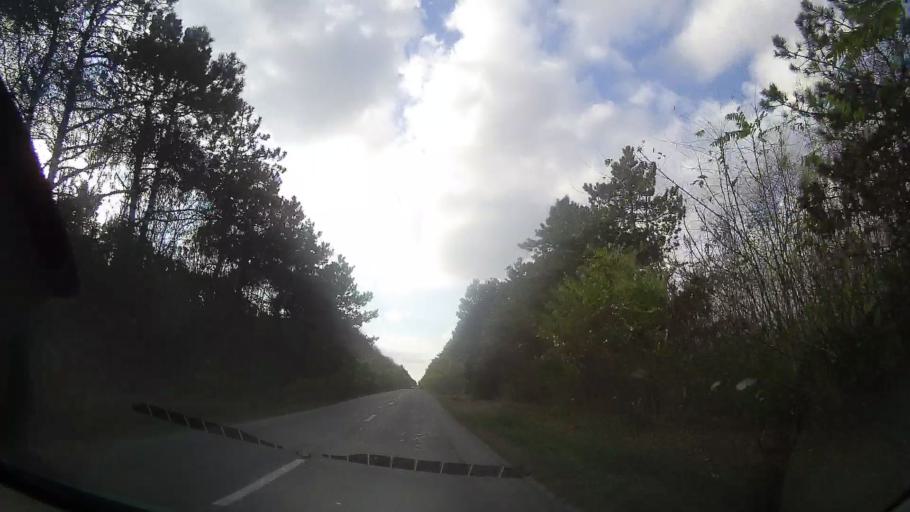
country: RO
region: Constanta
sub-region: Comuna Negru Voda
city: Negru Voda
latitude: 43.8194
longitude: 28.2617
